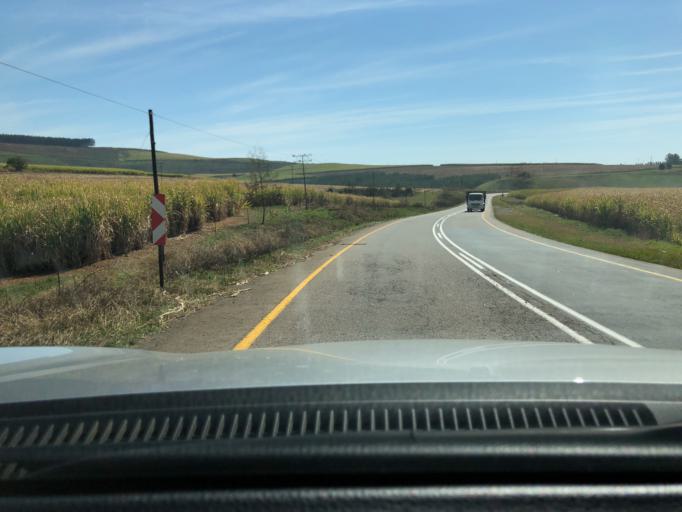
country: ZA
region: KwaZulu-Natal
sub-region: uMgungundlovu District Municipality
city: Richmond
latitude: -29.8059
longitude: 30.3431
